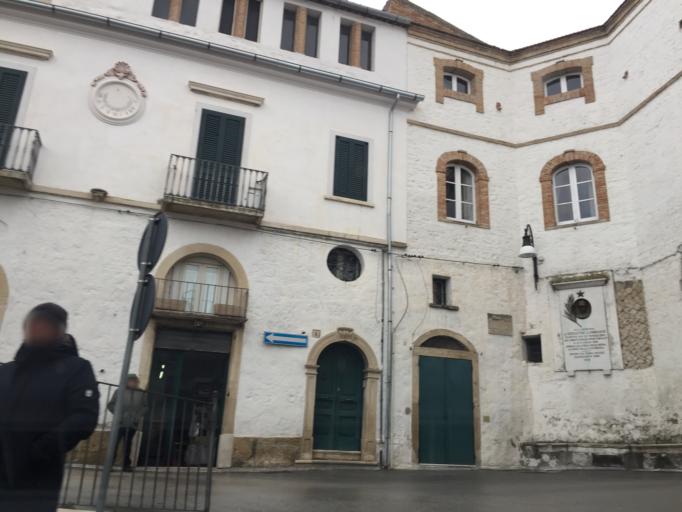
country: IT
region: Apulia
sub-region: Provincia di Foggia
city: Bovino
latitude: 41.2506
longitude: 15.3409
